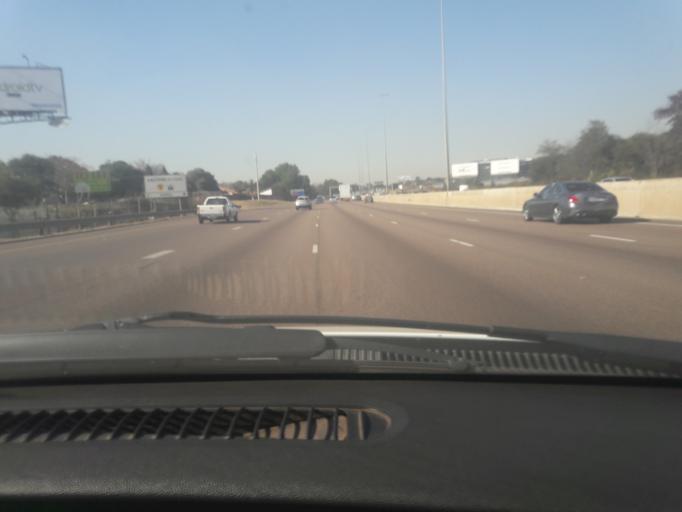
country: ZA
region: Gauteng
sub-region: City of Tshwane Metropolitan Municipality
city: Centurion
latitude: -25.8635
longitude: 28.2010
